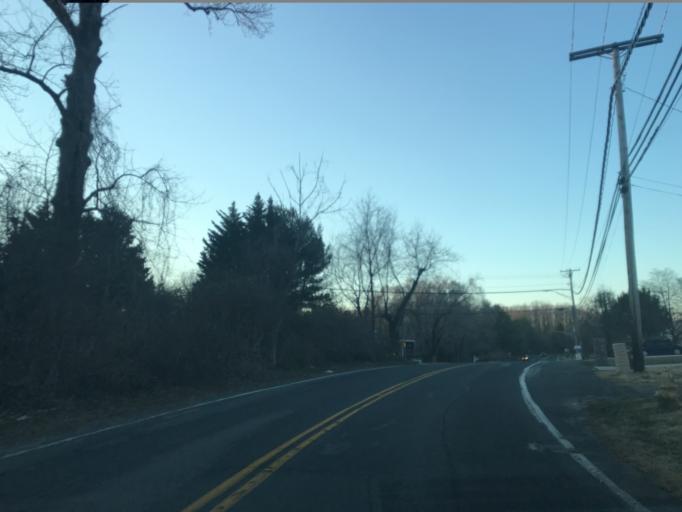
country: US
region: Maryland
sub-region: Anne Arundel County
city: Arnold
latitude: 39.0356
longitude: -76.4926
